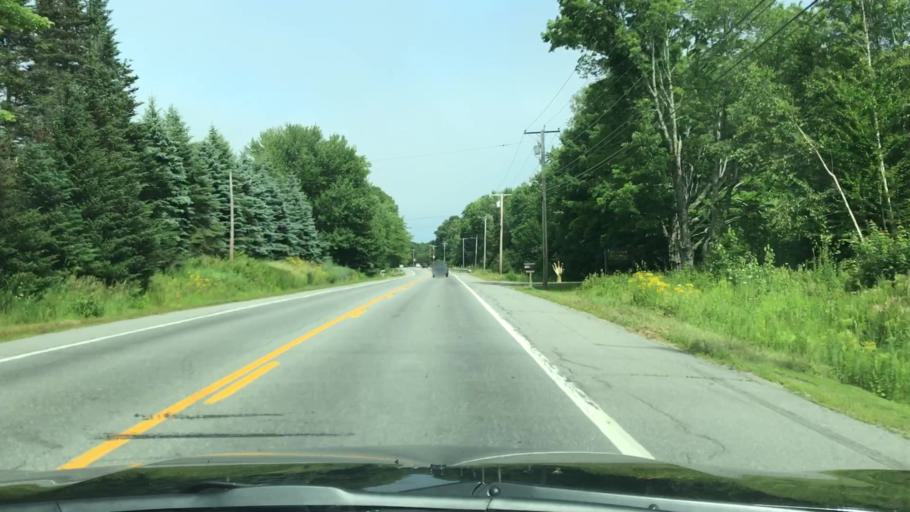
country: US
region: Maine
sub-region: Waldo County
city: Belfast
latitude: 44.4344
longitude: -68.9506
